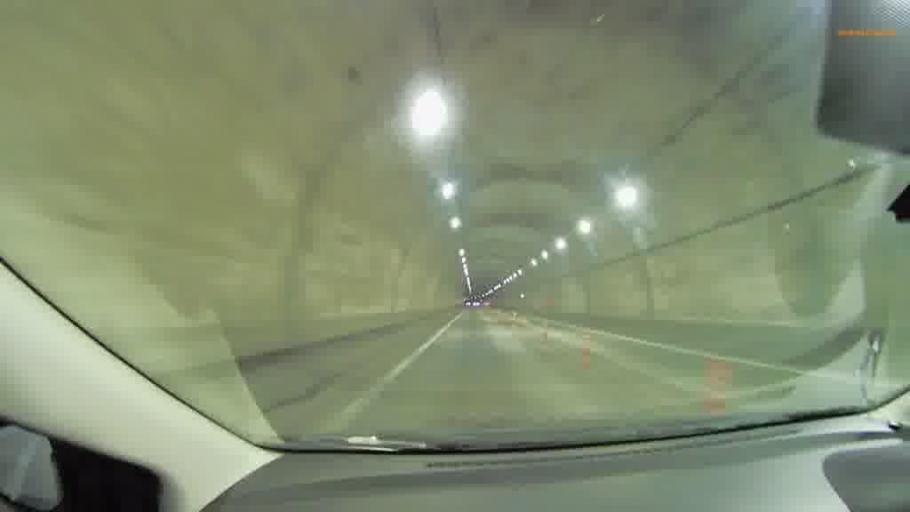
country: JP
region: Hokkaido
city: Kushiro
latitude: 43.0797
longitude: 144.0305
